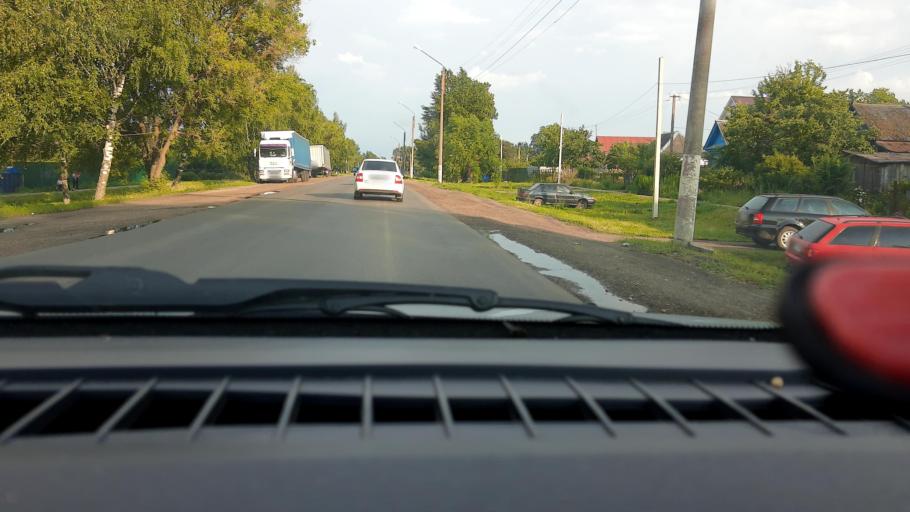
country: RU
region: Nizjnij Novgorod
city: Shatki
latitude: 55.1960
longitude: 44.1046
